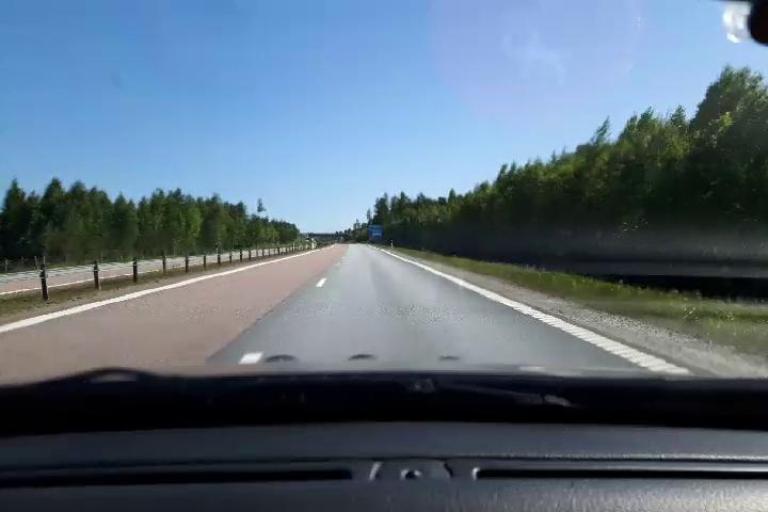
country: SE
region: Gaevleborg
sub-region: Hudiksvalls Kommun
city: Iggesund
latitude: 61.5253
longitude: 16.9734
